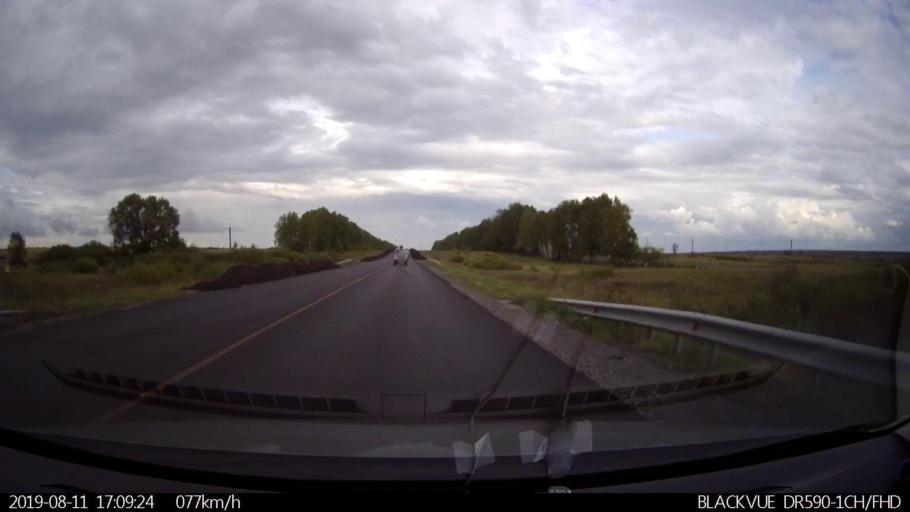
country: RU
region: Ulyanovsk
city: Mayna
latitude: 54.2962
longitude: 47.8555
